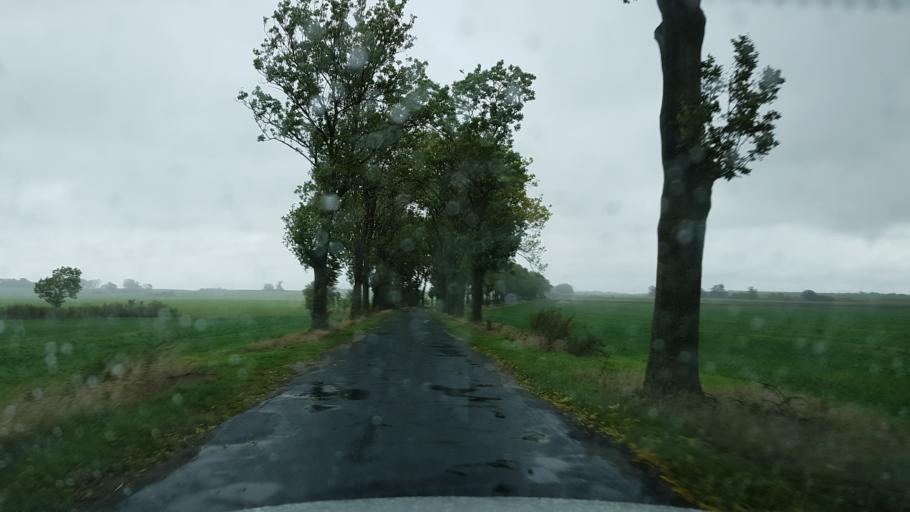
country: PL
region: West Pomeranian Voivodeship
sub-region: Powiat pyrzycki
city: Kozielice
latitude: 53.0427
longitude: 14.8586
